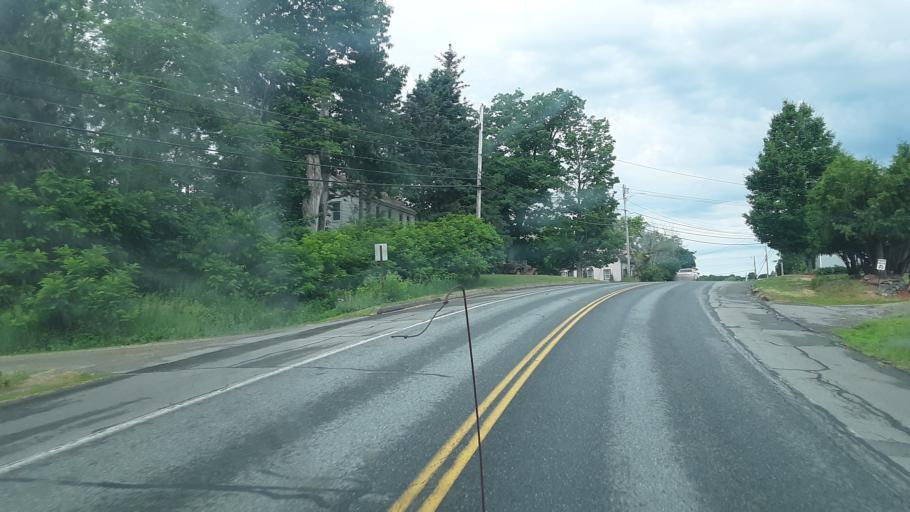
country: US
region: Maine
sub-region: Penobscot County
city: Eddington
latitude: 44.8179
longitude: -68.7089
